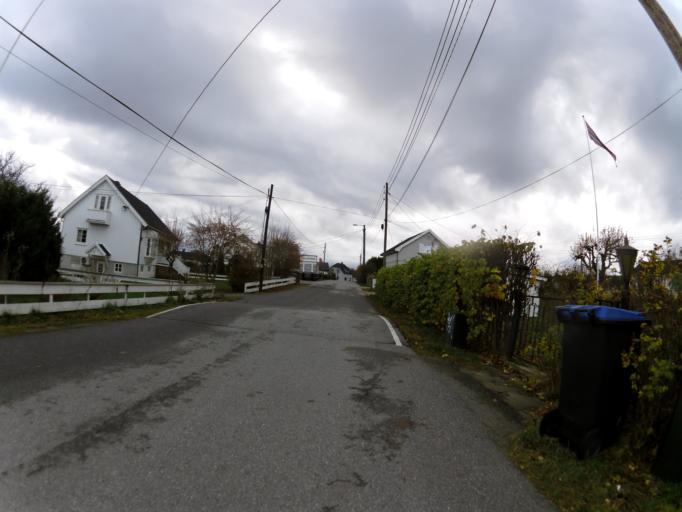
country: NO
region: Ostfold
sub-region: Sarpsborg
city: Sarpsborg
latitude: 59.2643
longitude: 11.0157
